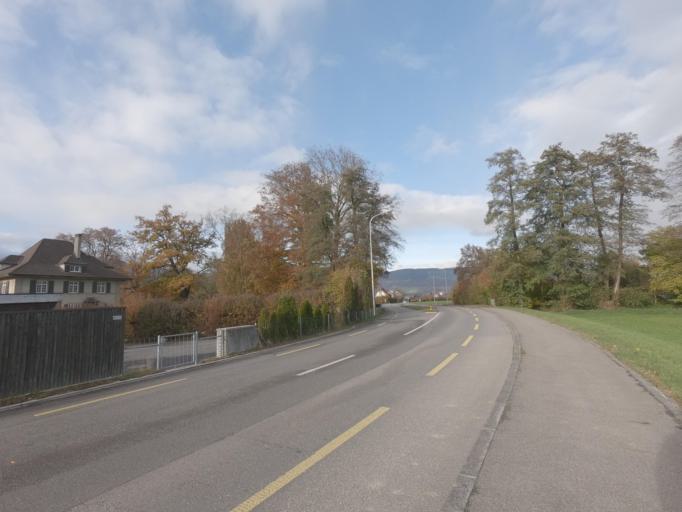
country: CH
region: Solothurn
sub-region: Bezirk Wasseramt
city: Derendingen
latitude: 47.2050
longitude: 7.5839
